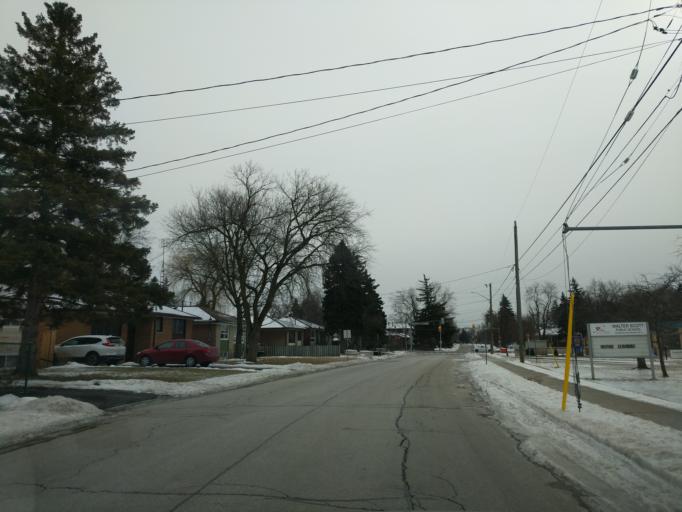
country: CA
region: Ontario
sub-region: York
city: Richmond Hill
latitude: 43.8758
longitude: -79.4215
